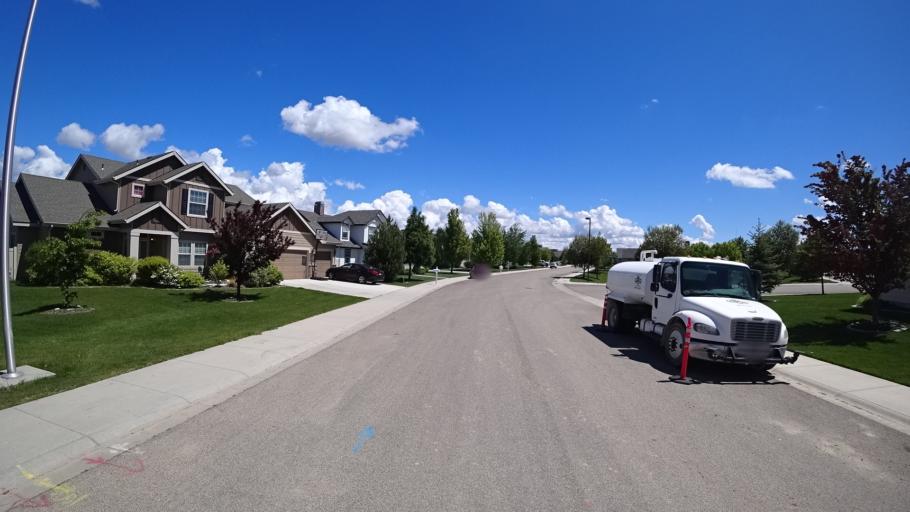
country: US
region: Idaho
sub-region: Ada County
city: Kuna
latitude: 43.5132
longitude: -116.4325
